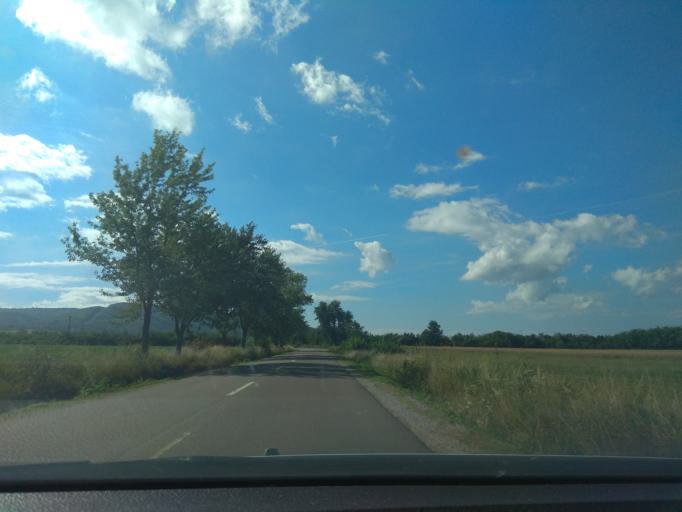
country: HU
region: Heves
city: Belapatfalva
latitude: 48.0558
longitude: 20.3303
